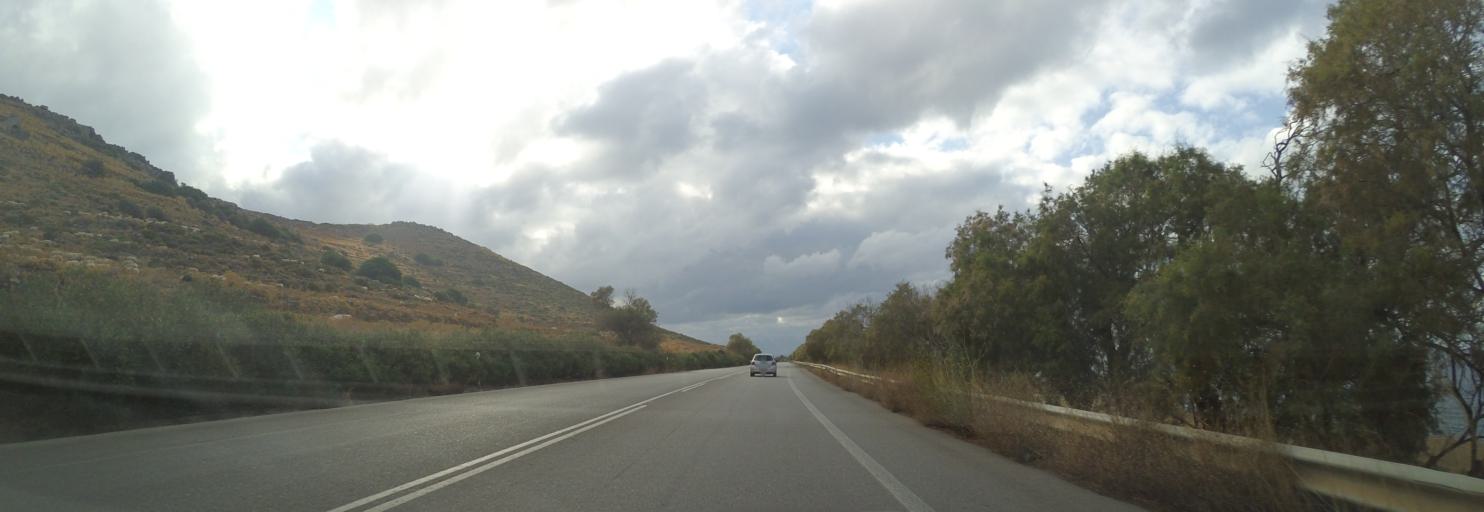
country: GR
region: Crete
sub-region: Nomos Rethymnis
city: Panormos
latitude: 35.4178
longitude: 24.6724
